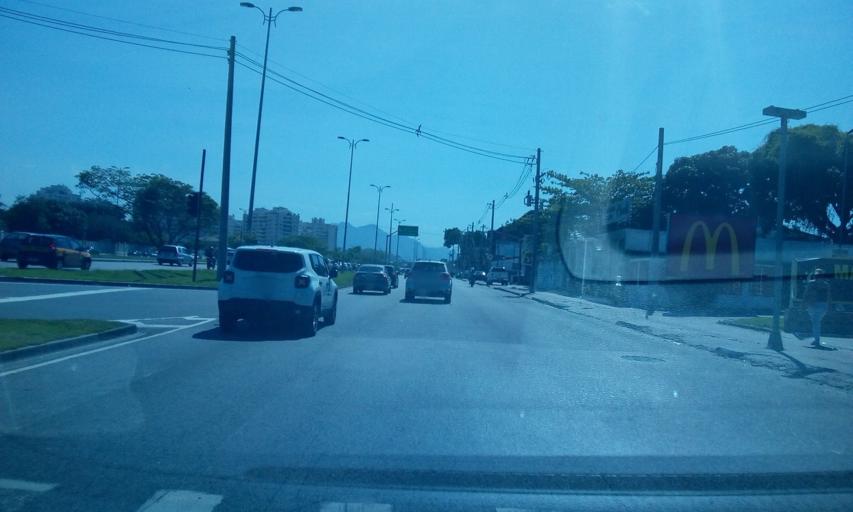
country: BR
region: Rio de Janeiro
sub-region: Nilopolis
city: Nilopolis
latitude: -23.0124
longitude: -43.4576
